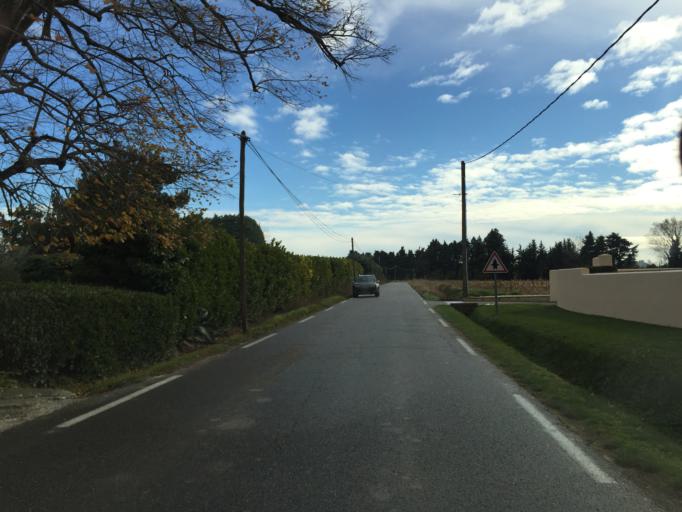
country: FR
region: Provence-Alpes-Cote d'Azur
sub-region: Departement du Vaucluse
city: Althen-des-Paluds
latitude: 43.9731
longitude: 4.9772
